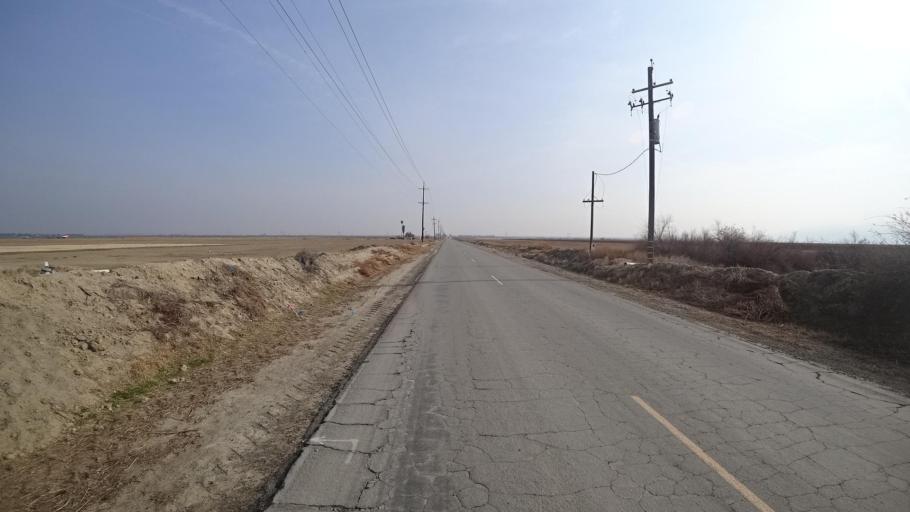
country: US
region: California
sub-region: Kern County
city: Greenfield
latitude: 35.0948
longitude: -119.0743
